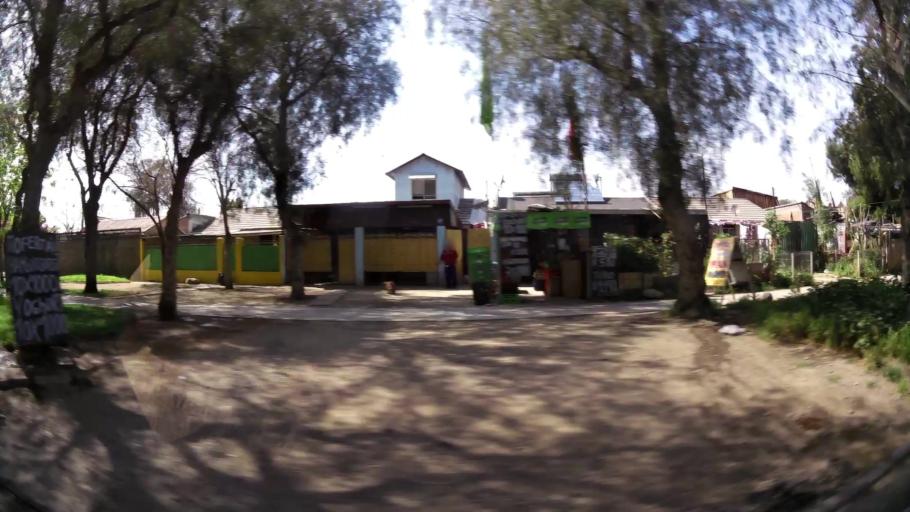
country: CL
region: Santiago Metropolitan
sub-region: Provincia de Santiago
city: Lo Prado
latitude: -33.4340
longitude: -70.7626
